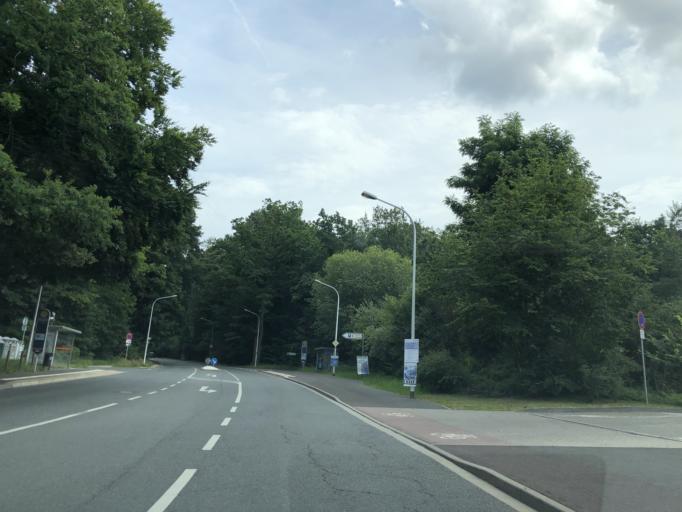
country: DE
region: Hesse
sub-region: Regierungsbezirk Darmstadt
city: Darmstadt
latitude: 49.8512
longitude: 8.6618
